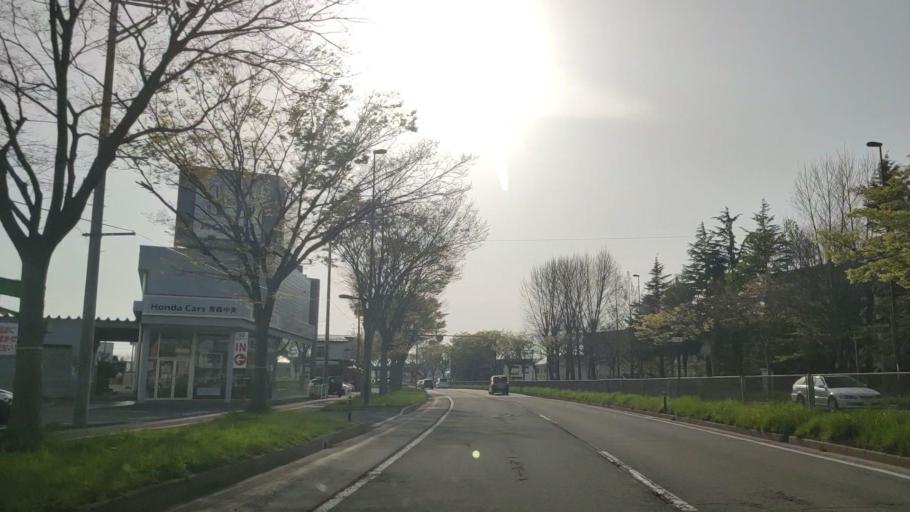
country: JP
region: Aomori
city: Aomori Shi
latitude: 40.8284
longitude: 140.7874
